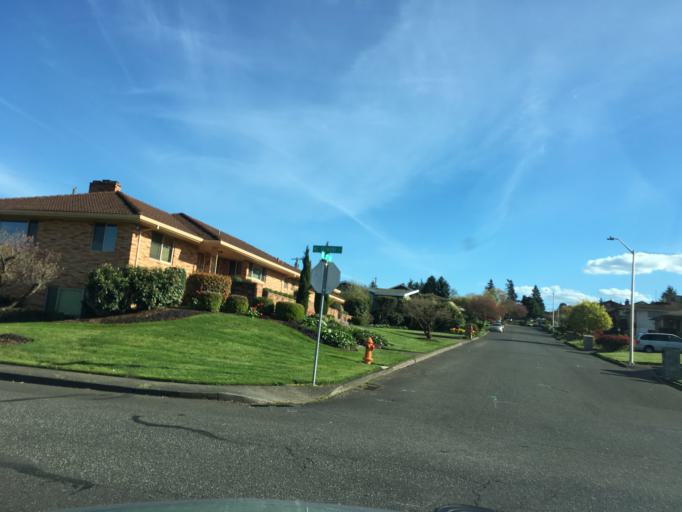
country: US
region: Oregon
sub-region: Multnomah County
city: Lents
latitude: 45.5481
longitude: -122.5321
